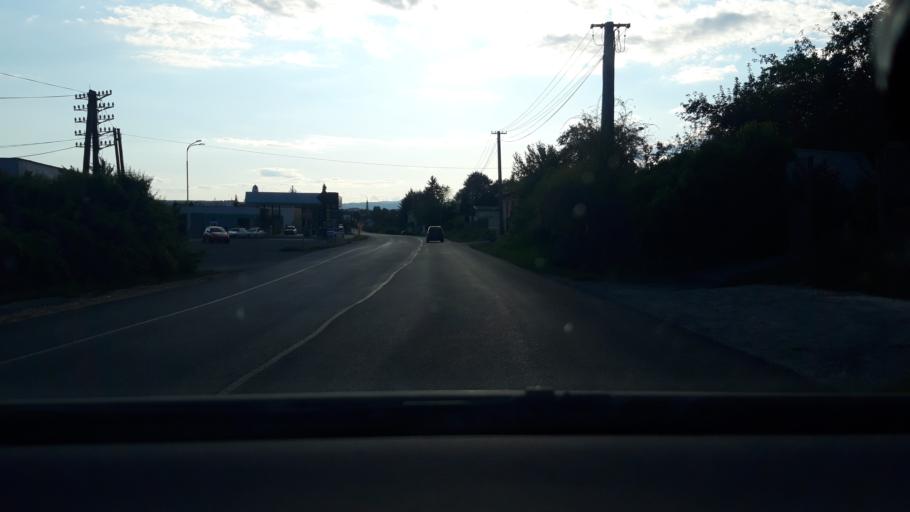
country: SK
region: Banskobystricky
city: Lucenec
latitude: 48.3275
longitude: 19.6912
